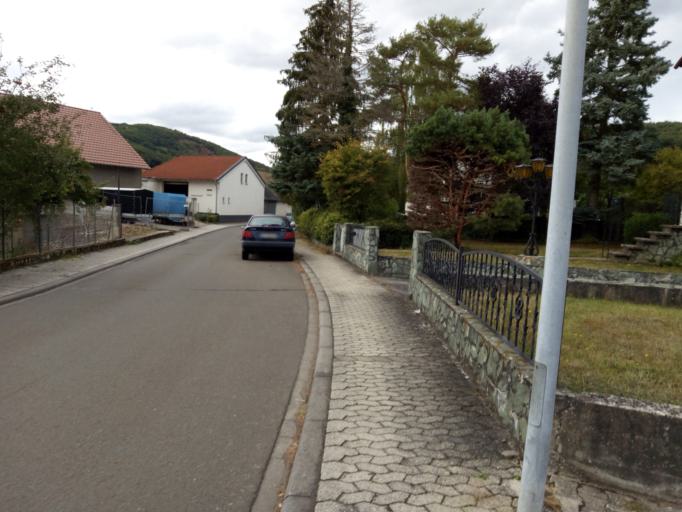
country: DE
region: Rheinland-Pfalz
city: Roth
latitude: 49.9267
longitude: 7.8013
